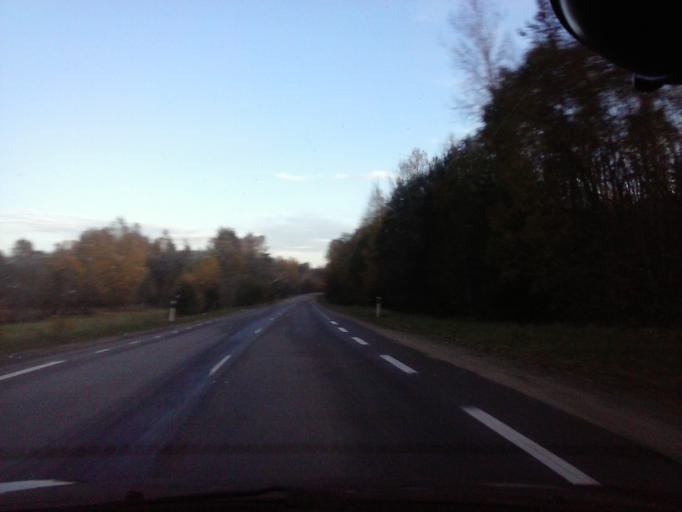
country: EE
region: Harju
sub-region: Nissi vald
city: Turba
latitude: 58.9159
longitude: 24.1959
